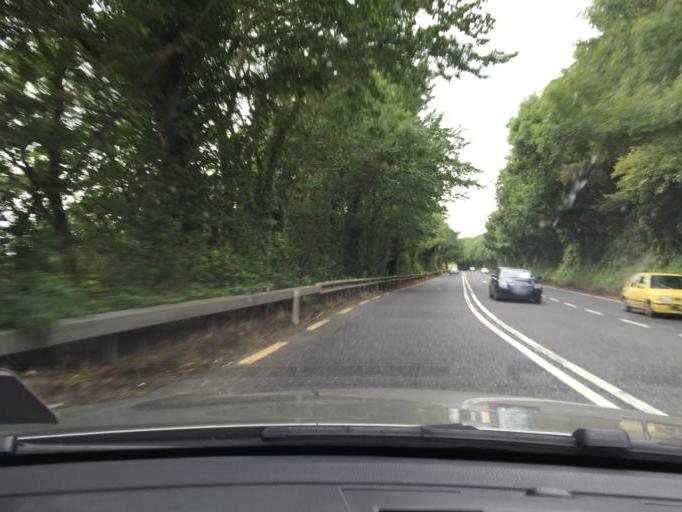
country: IE
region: Munster
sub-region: Waterford
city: Dungarvan
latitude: 52.1143
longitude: -7.5593
